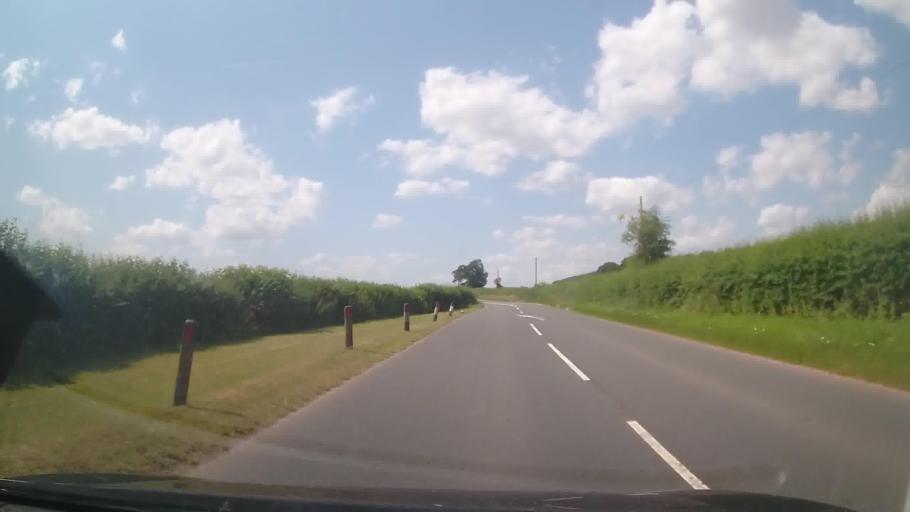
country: GB
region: England
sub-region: Herefordshire
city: Ocle Pychard
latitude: 52.1447
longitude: -2.6254
